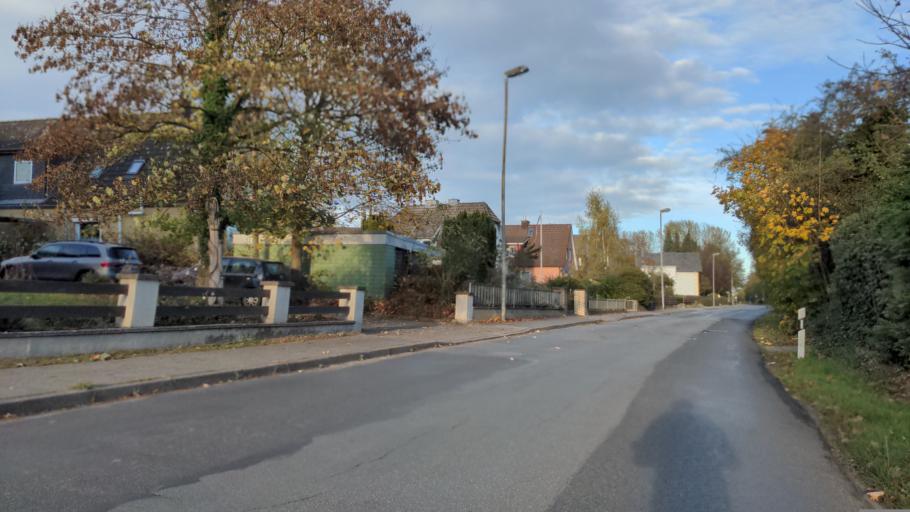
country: DE
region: Schleswig-Holstein
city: Reinfeld
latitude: 53.8383
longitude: 10.4940
